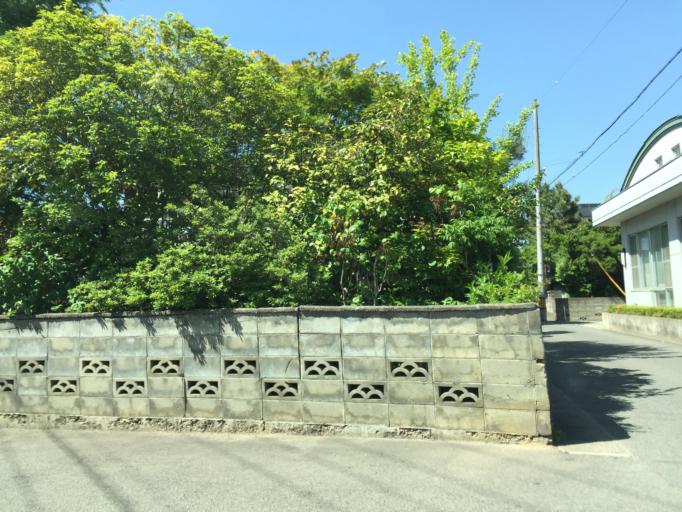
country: JP
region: Fukushima
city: Fukushima-shi
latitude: 37.7690
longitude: 140.4499
